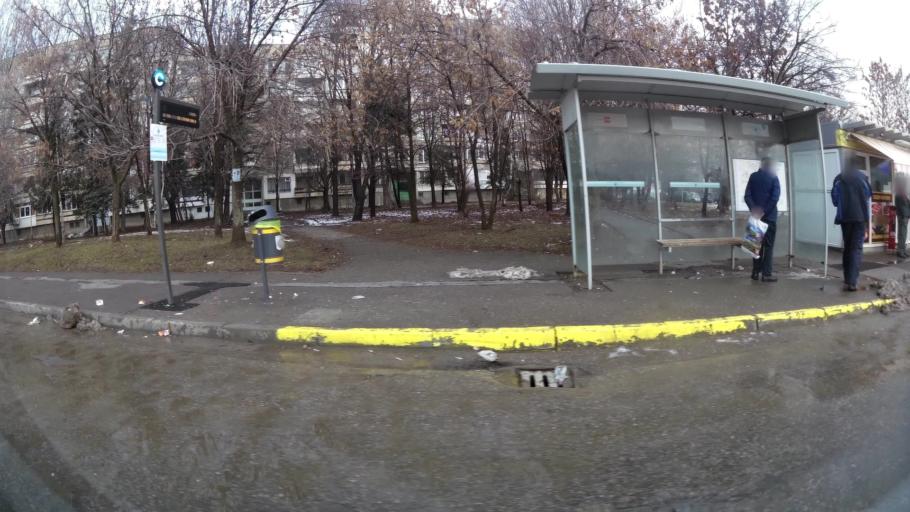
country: BG
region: Sofiya
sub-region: Obshtina Bozhurishte
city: Bozhurishte
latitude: 42.7087
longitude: 23.2516
